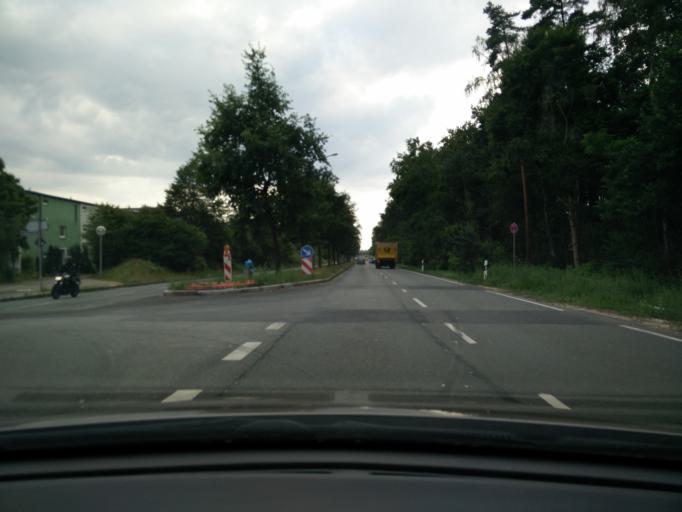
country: DE
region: Bavaria
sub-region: Regierungsbezirk Mittelfranken
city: Nuernberg
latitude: 49.4205
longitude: 11.1298
